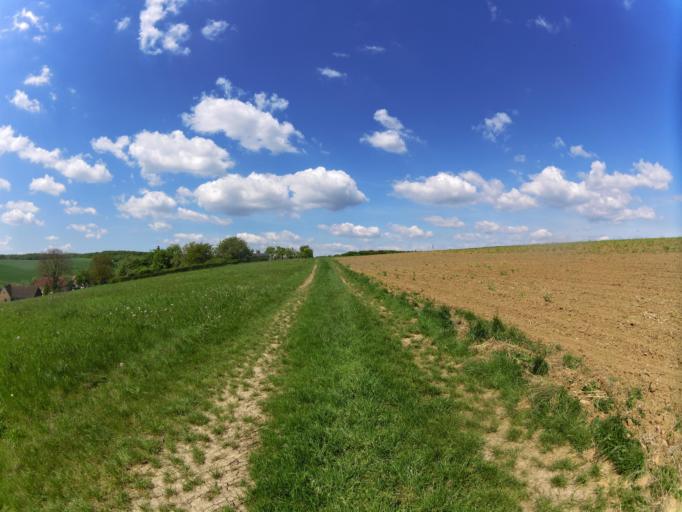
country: DE
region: Bavaria
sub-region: Regierungsbezirk Unterfranken
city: Unterpleichfeld
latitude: 49.8856
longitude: 10.0119
